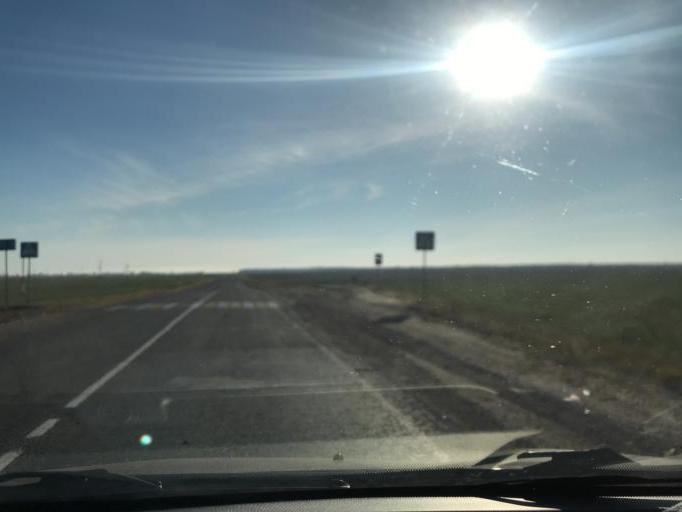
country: BY
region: Gomel
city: Brahin
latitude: 51.7921
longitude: 30.1701
